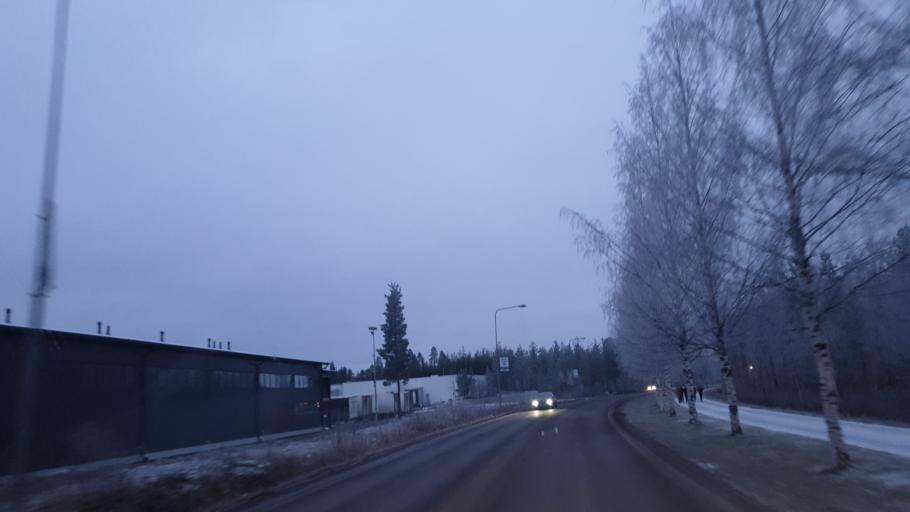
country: FI
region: Southern Ostrobothnia
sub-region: Seinaejoki
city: Nurmo
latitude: 62.7797
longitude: 22.8968
